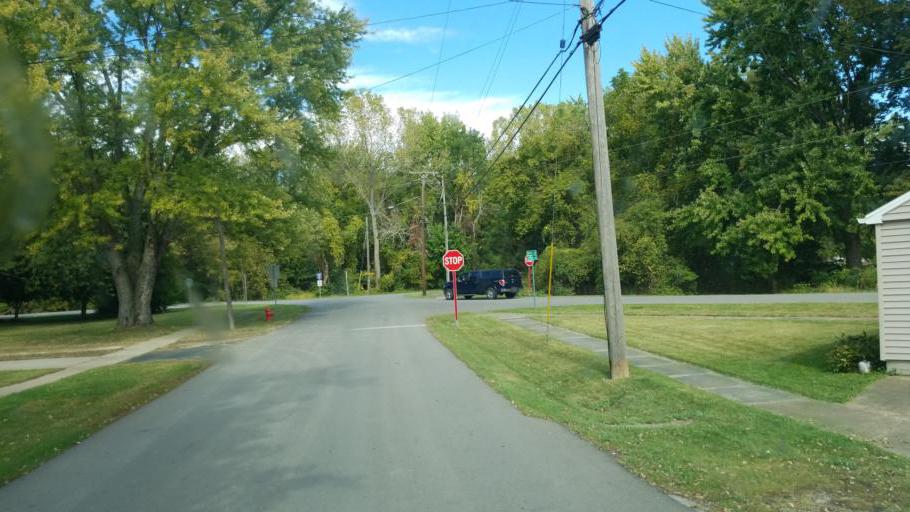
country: US
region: Ohio
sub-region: Erie County
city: Huron
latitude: 41.3919
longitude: -82.5458
